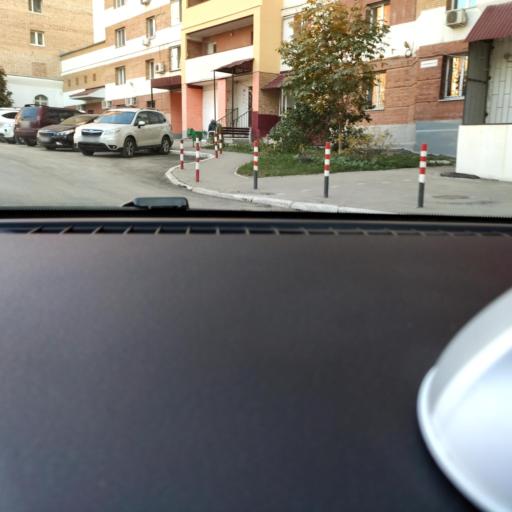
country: RU
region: Samara
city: Samara
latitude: 53.1973
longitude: 50.1467
